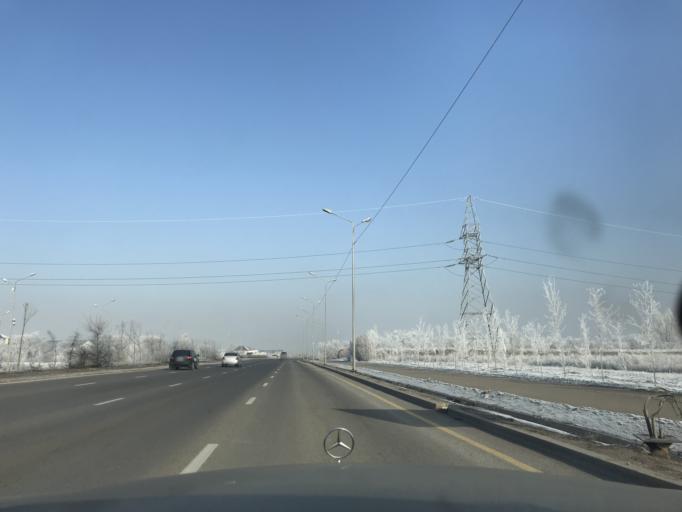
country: KZ
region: Almaty Oblysy
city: Burunday
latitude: 43.3331
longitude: 76.8335
